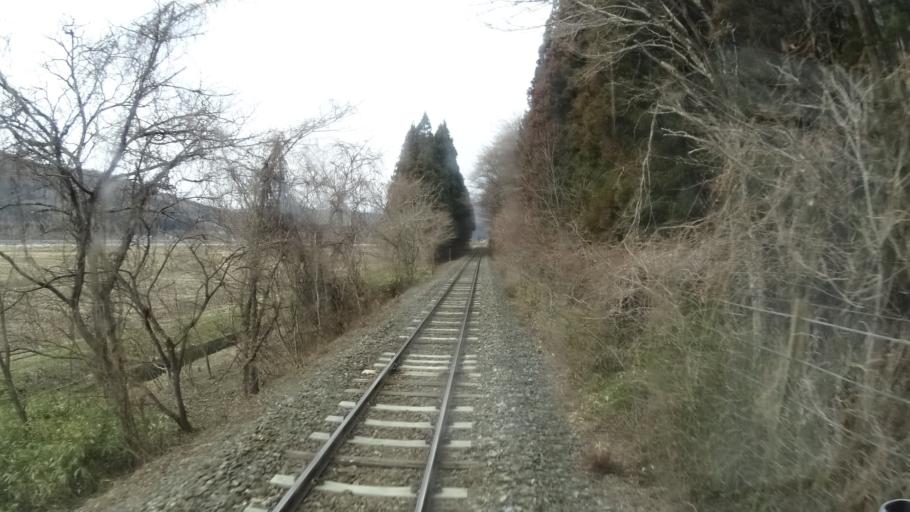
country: JP
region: Iwate
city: Tono
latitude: 39.3085
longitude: 141.4209
